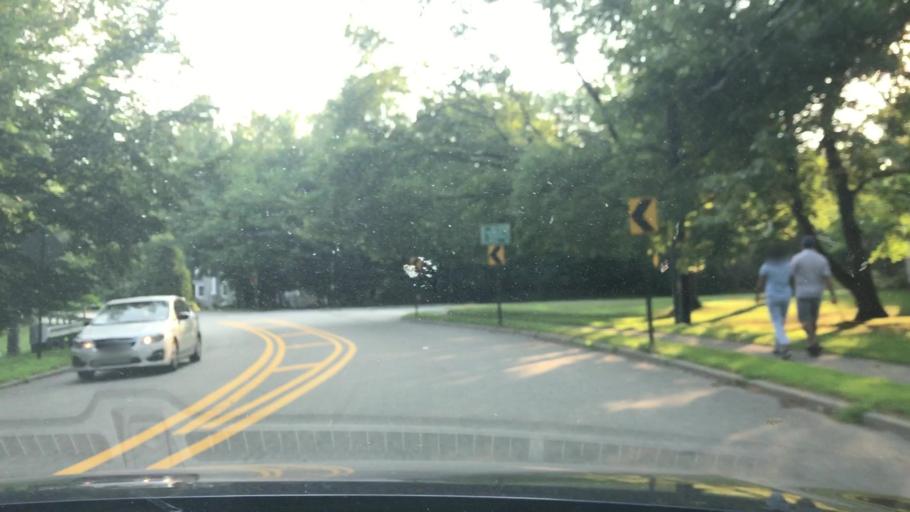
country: US
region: New Jersey
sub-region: Bergen County
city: River Vale
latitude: 40.9937
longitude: -74.0199
